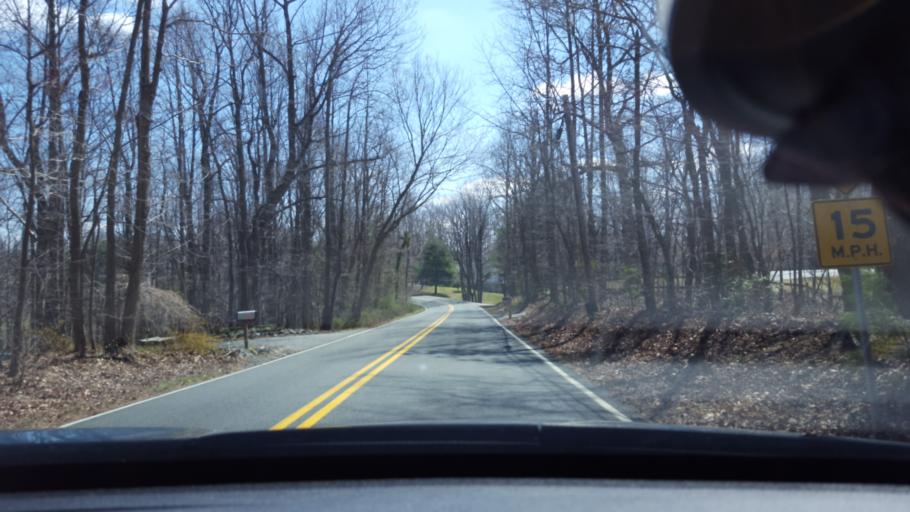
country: US
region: Maryland
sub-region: Calvert County
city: Chesapeake Beach
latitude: 38.6280
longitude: -76.5249
